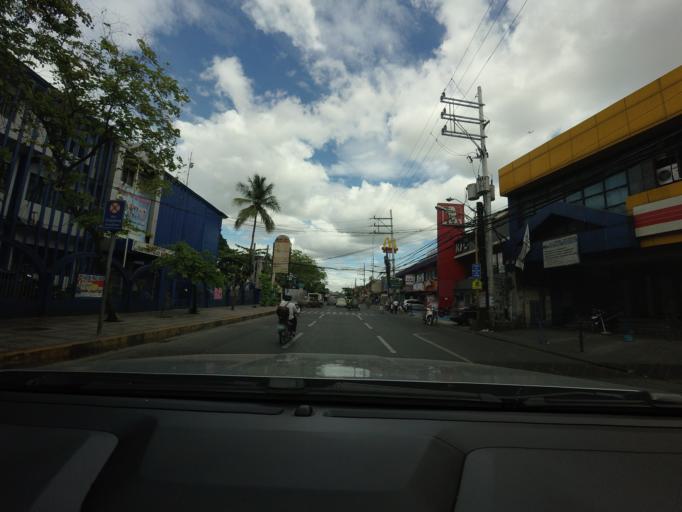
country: PH
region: Calabarzon
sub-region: Province of Rizal
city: Pateros
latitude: 14.5587
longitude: 121.0817
